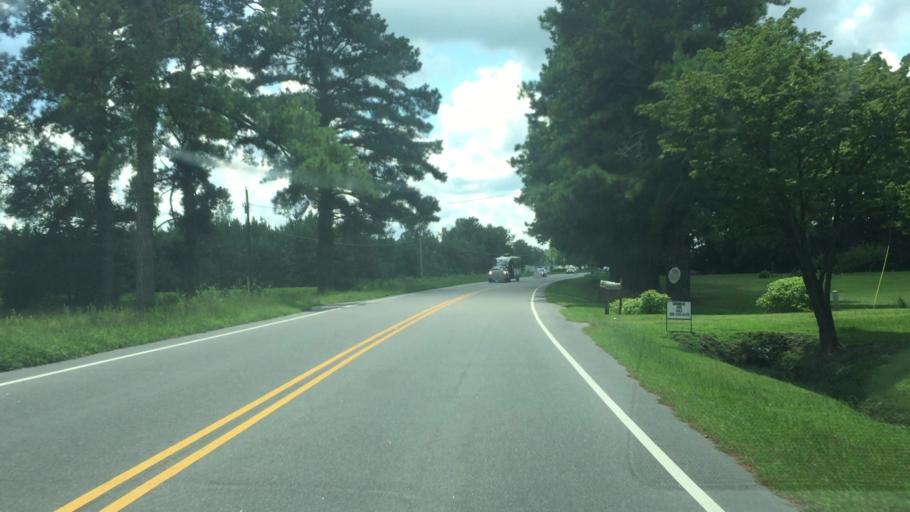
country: US
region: North Carolina
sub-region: Columbus County
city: Chadbourn
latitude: 34.2727
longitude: -78.8128
